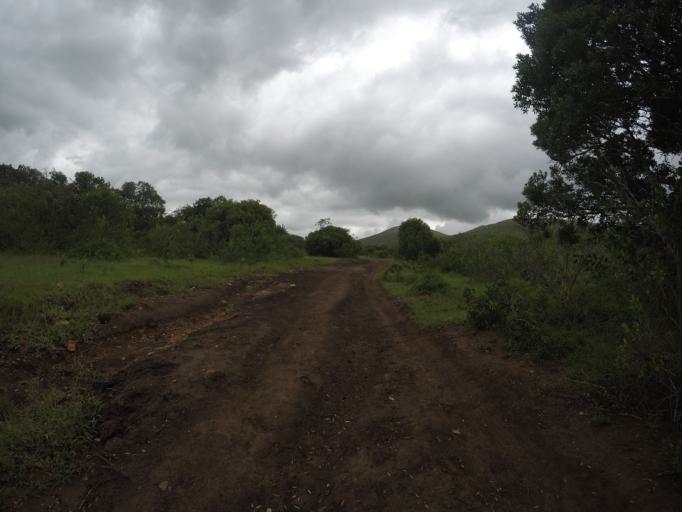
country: ZA
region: KwaZulu-Natal
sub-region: uThungulu District Municipality
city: Empangeni
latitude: -28.5686
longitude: 31.8723
